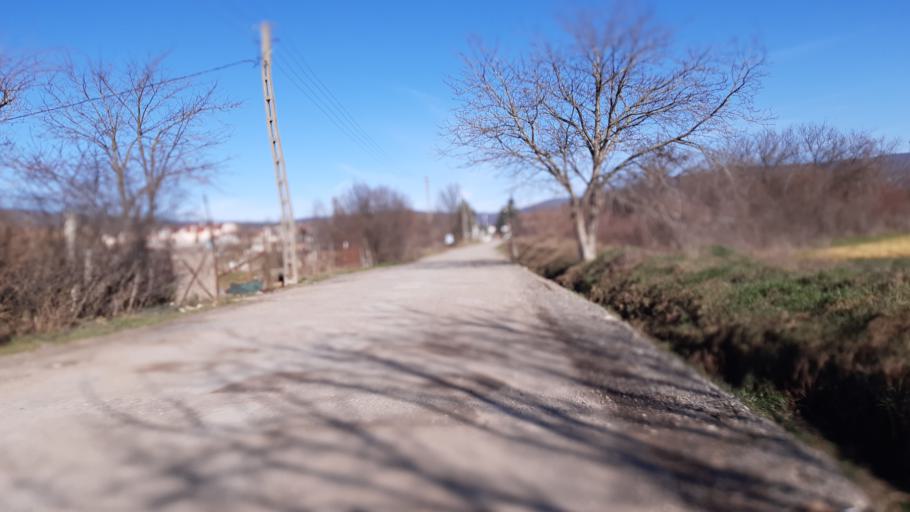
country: HU
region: Baranya
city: Pellerd
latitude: 46.0572
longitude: 18.1876
